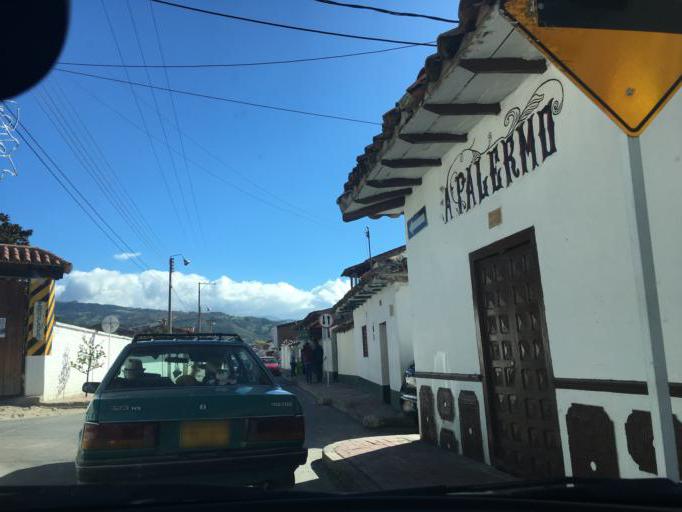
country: CO
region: Boyaca
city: Firavitoba
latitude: 5.6121
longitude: -72.9802
